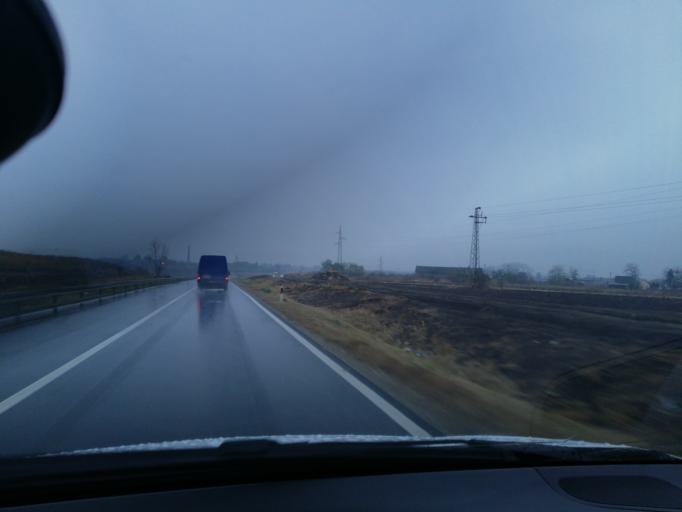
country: RS
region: Autonomna Pokrajina Vojvodina
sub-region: Sremski Okrug
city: Ruma
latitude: 45.0157
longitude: 19.8436
